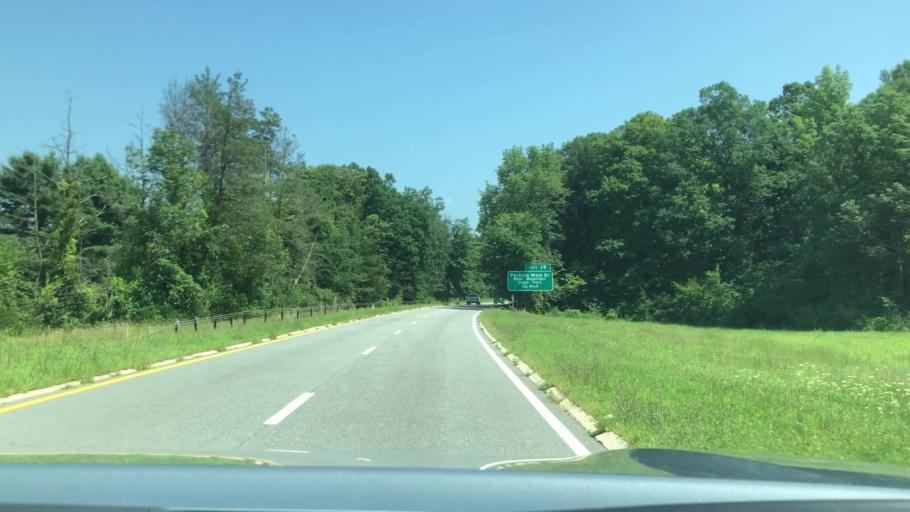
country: US
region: New York
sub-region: Orange County
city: Fort Montgomery
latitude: 41.3043
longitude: -74.0297
